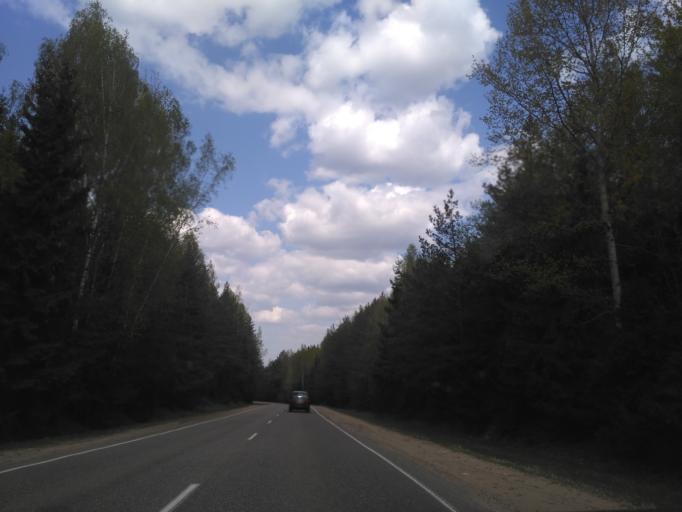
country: BY
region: Minsk
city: Il'ya
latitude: 54.4645
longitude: 27.2810
